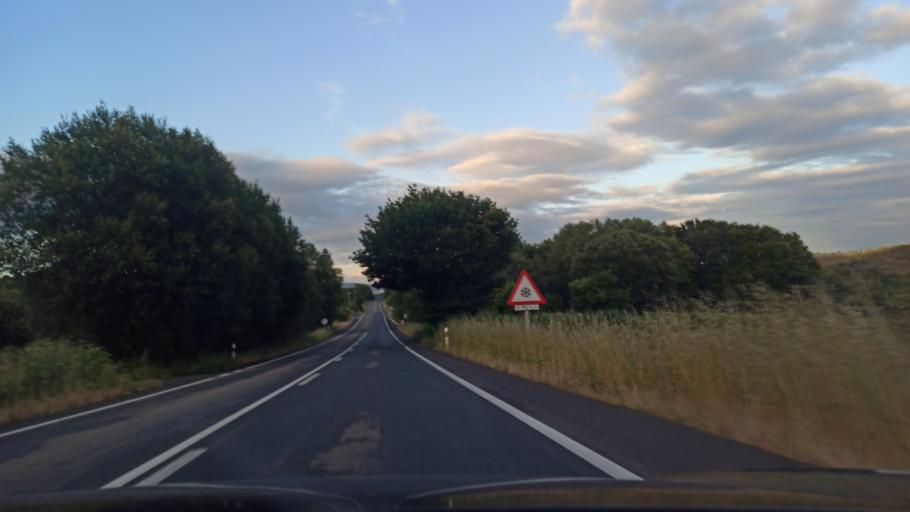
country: ES
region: Galicia
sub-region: Provincia de Lugo
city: Monterroso
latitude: 42.7740
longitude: -7.9539
